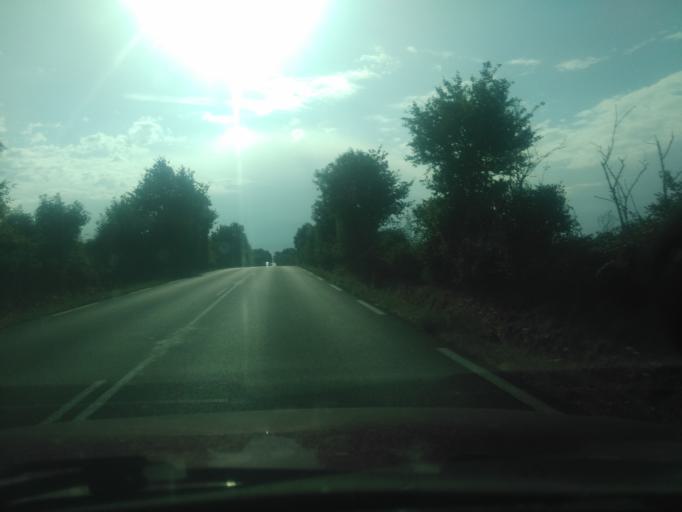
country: FR
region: Pays de la Loire
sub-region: Departement de la Vendee
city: Bazoges-en-Pareds
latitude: 46.6777
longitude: -0.9062
